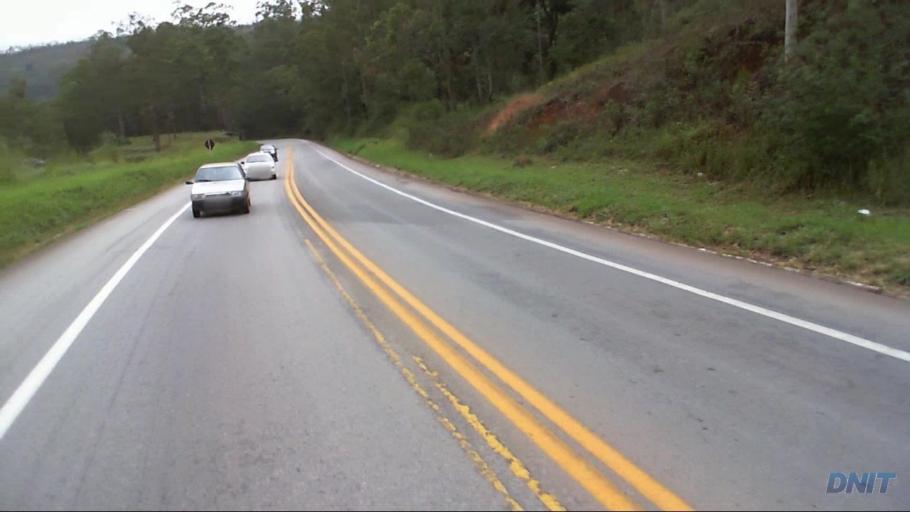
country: BR
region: Minas Gerais
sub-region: Joao Monlevade
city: Joao Monlevade
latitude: -19.8499
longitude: -43.1435
